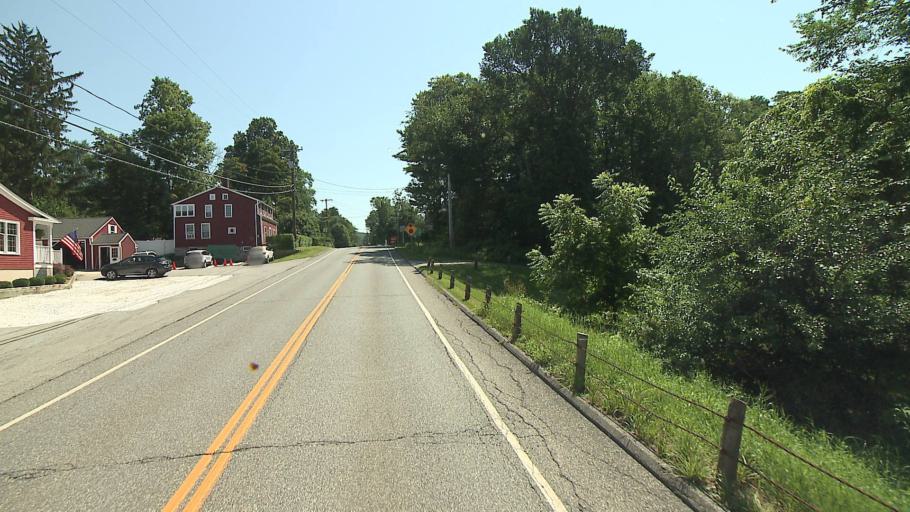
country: US
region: Connecticut
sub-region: Litchfield County
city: Kent
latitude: 41.8764
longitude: -73.4787
